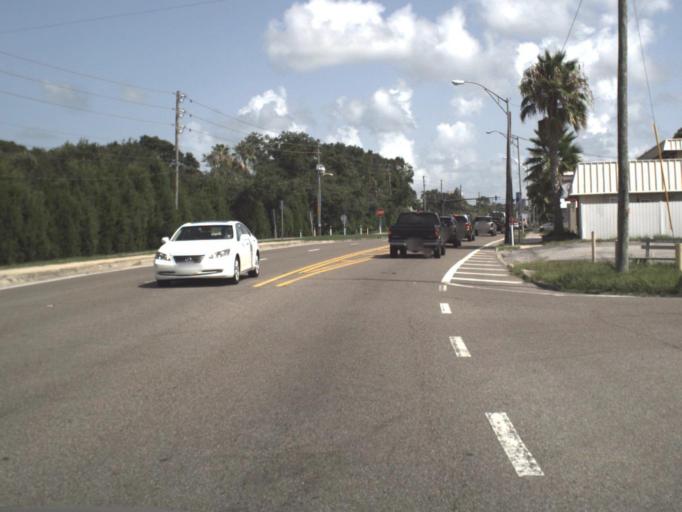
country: US
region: Florida
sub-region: Pinellas County
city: Belleair
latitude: 27.9425
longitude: -82.7999
